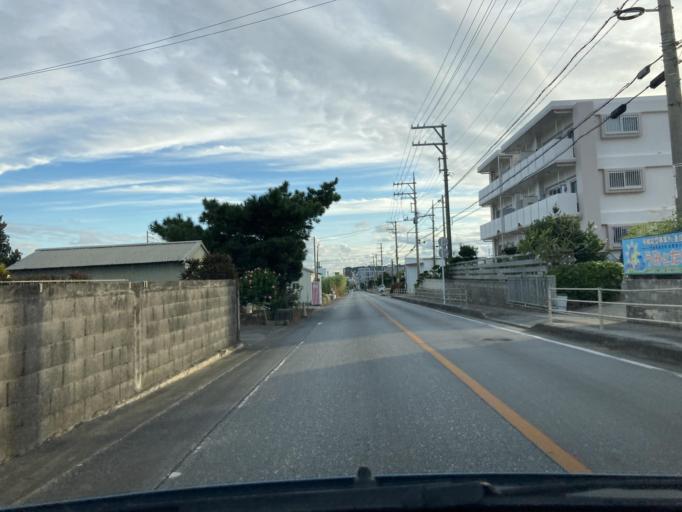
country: JP
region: Okinawa
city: Itoman
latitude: 26.1423
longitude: 127.6889
